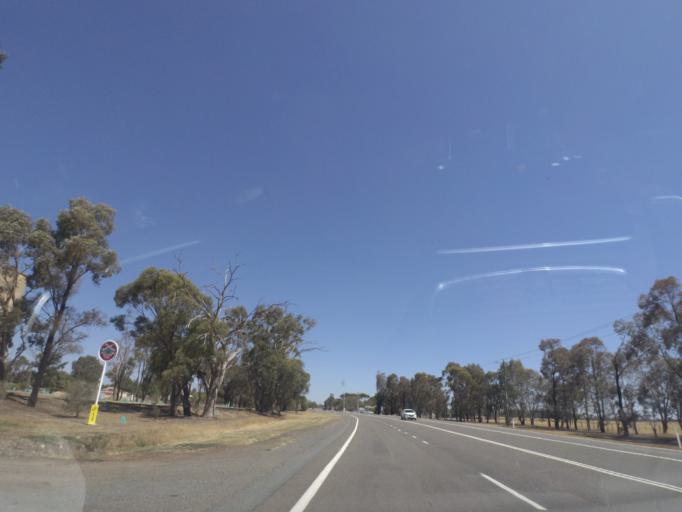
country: AU
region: Victoria
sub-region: Greater Shepparton
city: Shepparton
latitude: -36.2366
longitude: 145.4315
